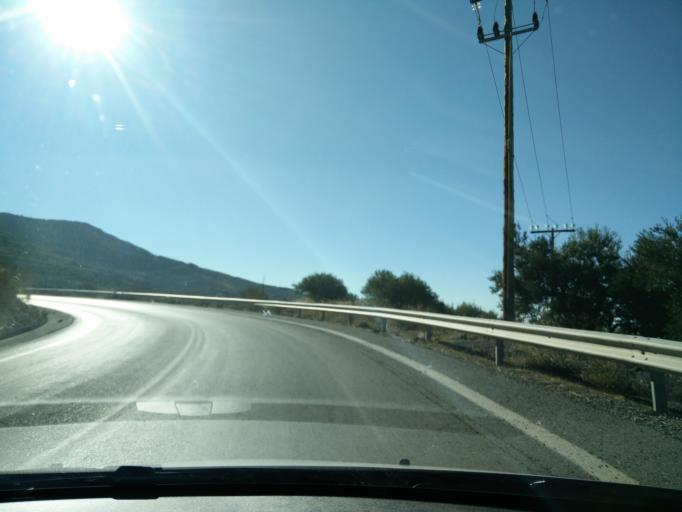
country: GR
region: Crete
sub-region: Nomos Irakleiou
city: Arkalochori
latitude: 35.0766
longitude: 25.3611
